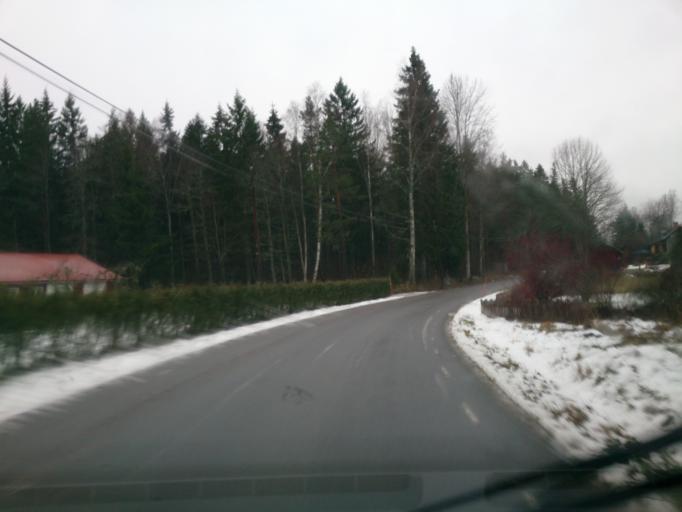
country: SE
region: OEstergoetland
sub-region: Atvidabergs Kommun
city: Atvidaberg
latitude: 58.2525
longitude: 16.1019
